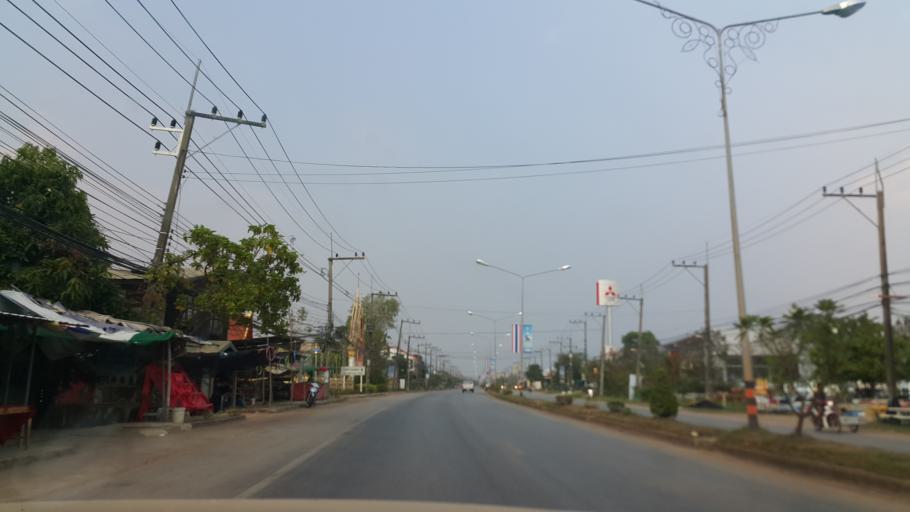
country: TH
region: Nakhon Phanom
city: That Phanom
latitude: 16.9599
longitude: 104.7258
